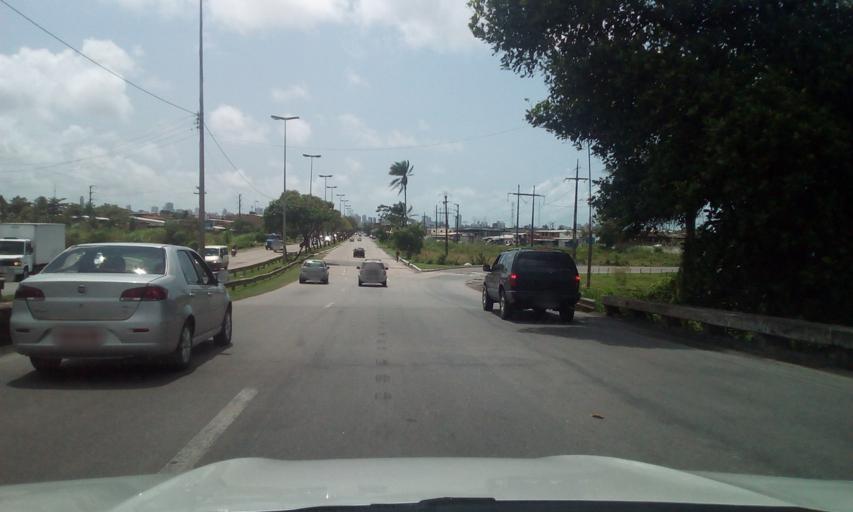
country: BR
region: Pernambuco
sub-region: Recife
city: Recife
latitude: -8.0664
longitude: -34.9412
